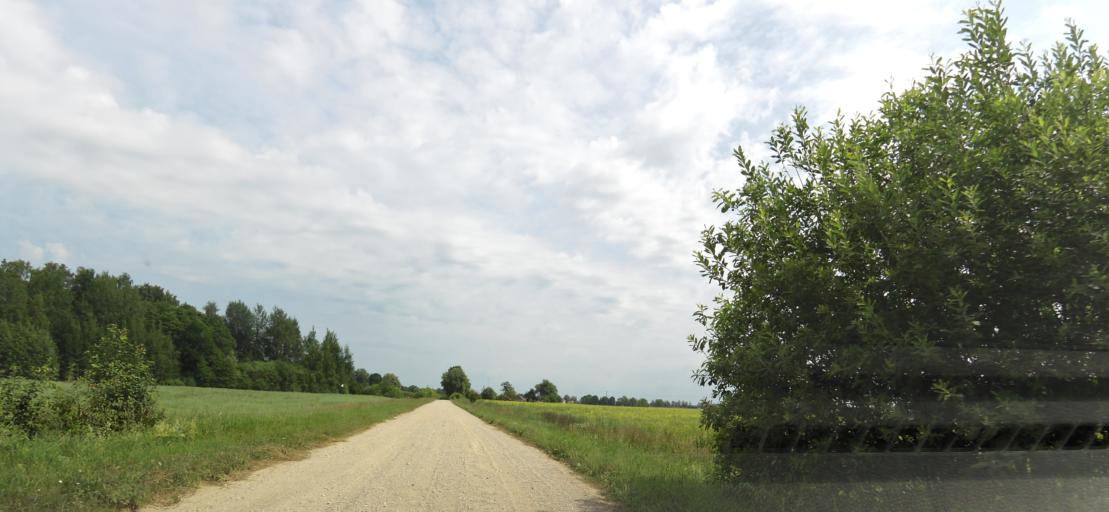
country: LT
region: Panevezys
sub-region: Birzai
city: Birzai
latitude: 56.3221
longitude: 24.6964
